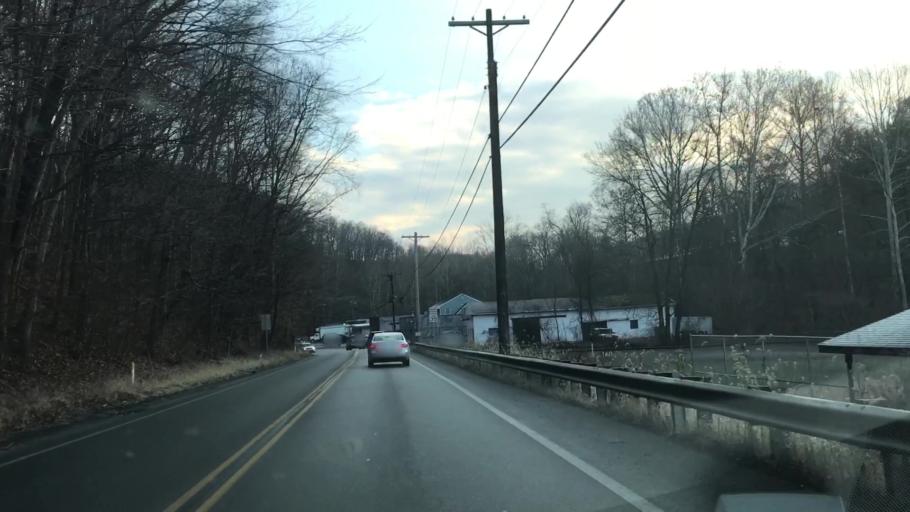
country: US
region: Pennsylvania
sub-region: Allegheny County
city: Ben Avon
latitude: 40.5226
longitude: -80.0827
